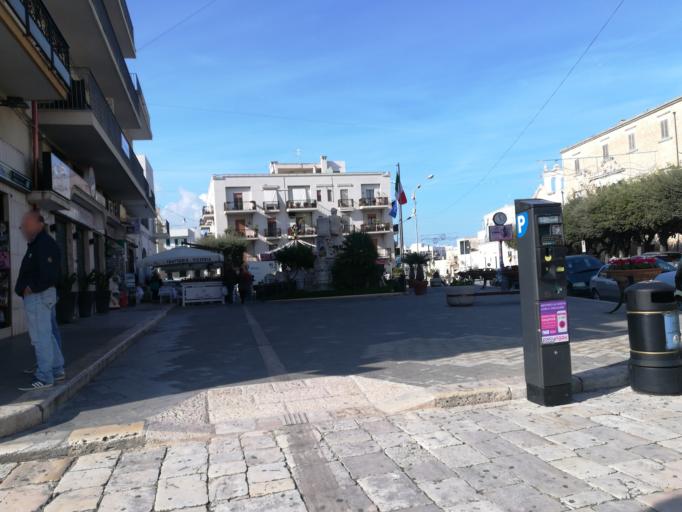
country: IT
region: Apulia
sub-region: Provincia di Bari
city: Polignano a Mare
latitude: 40.9950
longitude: 17.2195
